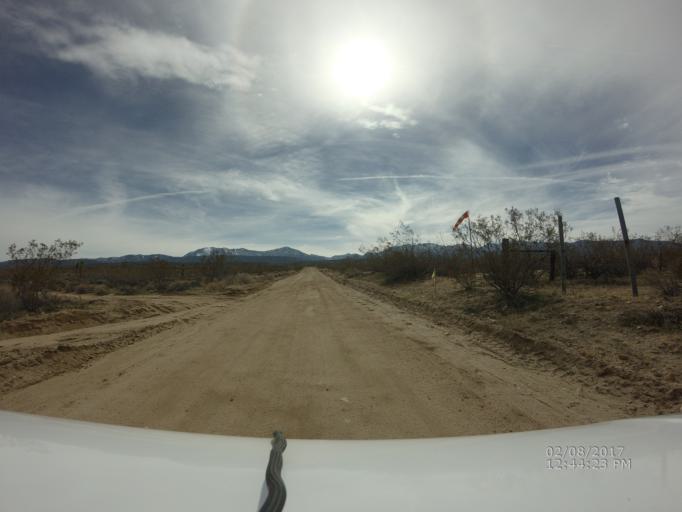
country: US
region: California
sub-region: Los Angeles County
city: Lake Los Angeles
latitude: 34.4842
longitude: -117.8178
